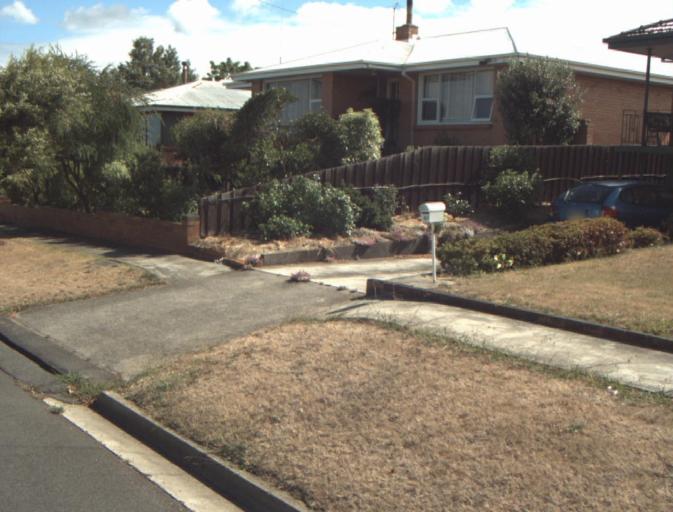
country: AU
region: Tasmania
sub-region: Launceston
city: Mayfield
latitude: -41.3856
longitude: 147.1244
